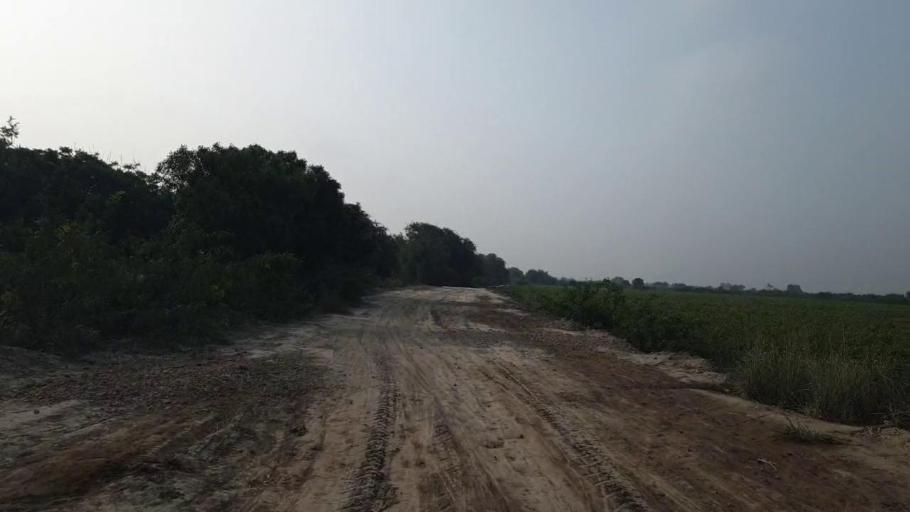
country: PK
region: Sindh
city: Tando Muhammad Khan
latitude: 25.1613
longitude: 68.5957
